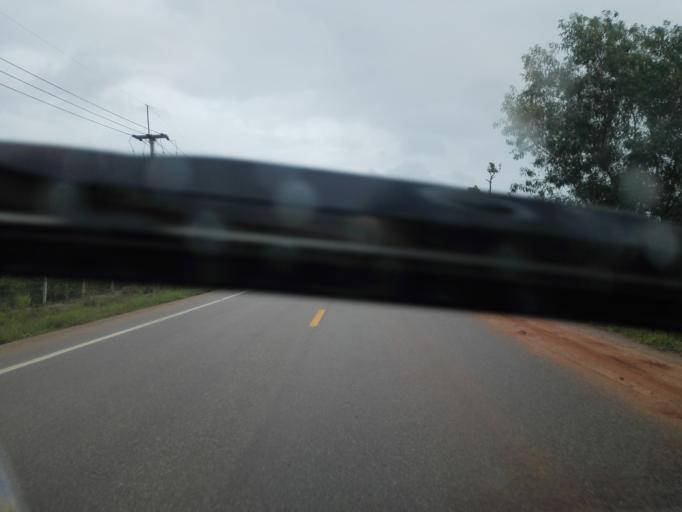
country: TH
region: Tak
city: Mae Sot
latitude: 16.6900
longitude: 98.4450
